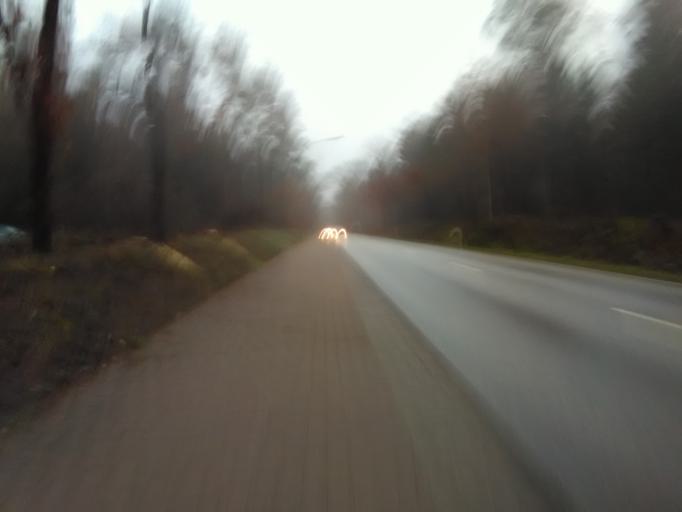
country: DE
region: Schleswig-Holstein
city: Norderstedt
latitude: 53.7206
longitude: 9.9690
